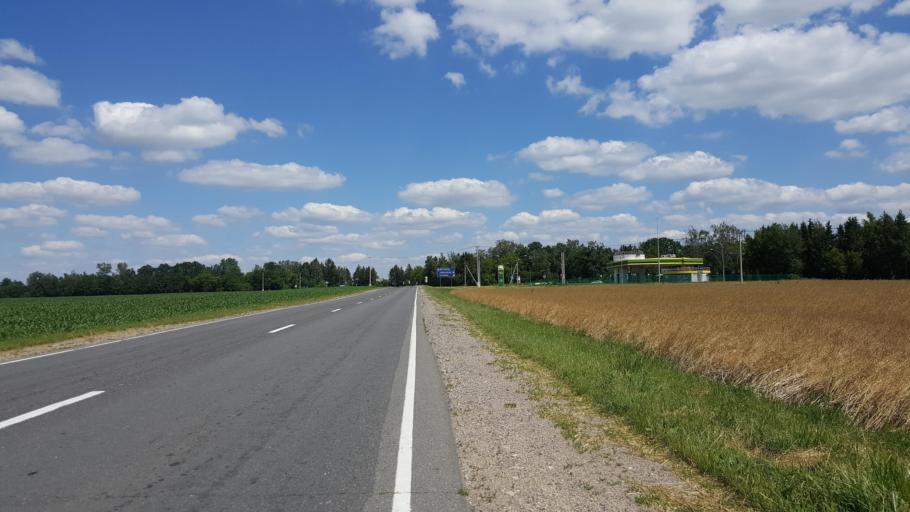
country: BY
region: Brest
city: Kamyanyets
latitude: 52.4090
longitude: 23.7865
